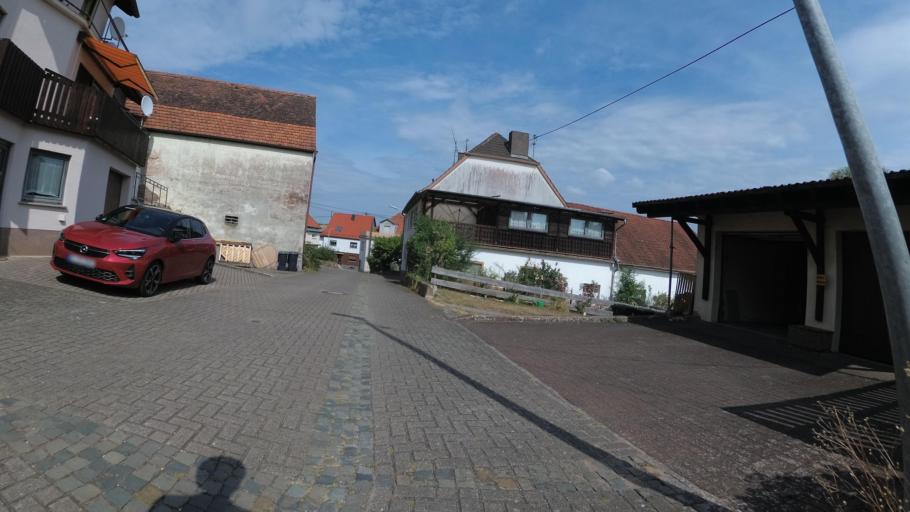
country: DE
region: Rheinland-Pfalz
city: Wahnwegen
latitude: 49.4836
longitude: 7.3749
